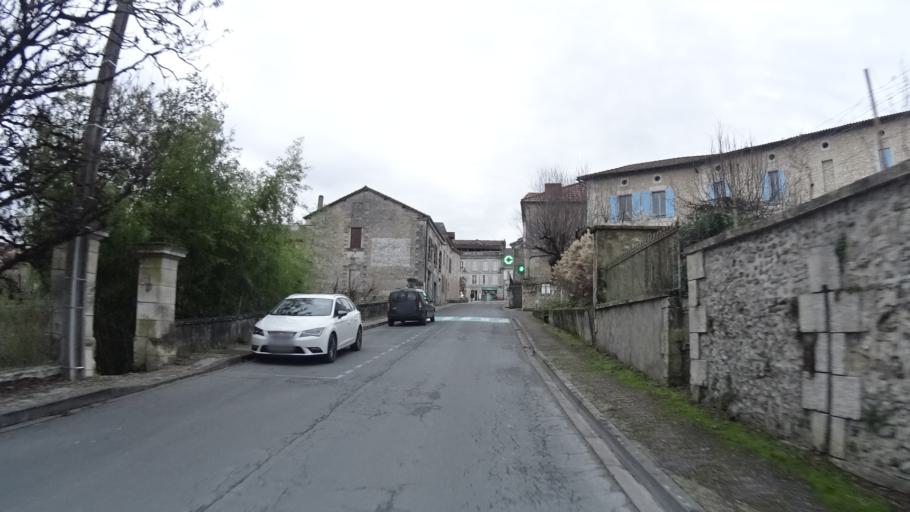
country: FR
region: Aquitaine
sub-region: Departement de la Dordogne
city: Saint-Aulaye
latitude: 45.2039
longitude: 0.1350
